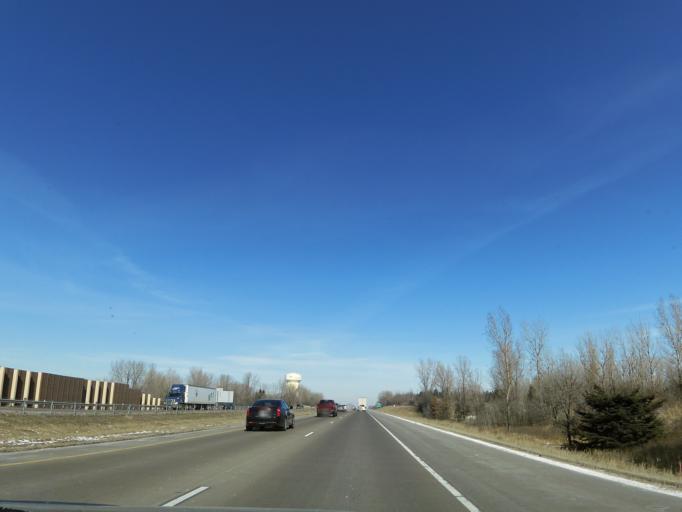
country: US
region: Minnesota
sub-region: Washington County
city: Oakdale
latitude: 44.9761
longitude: -92.9592
